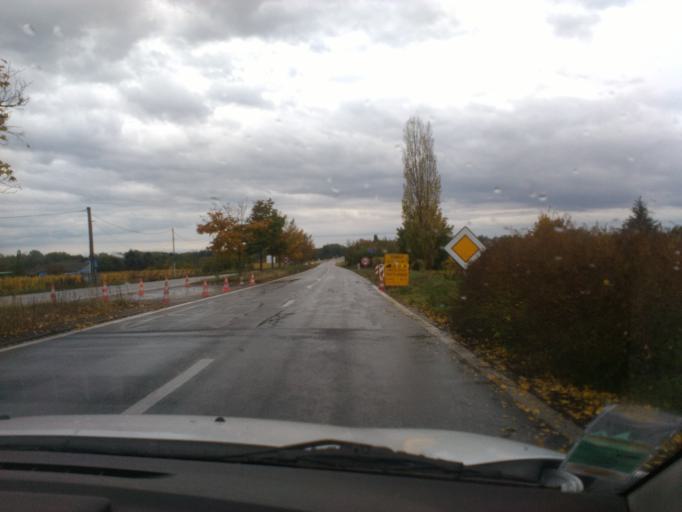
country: FR
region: Alsace
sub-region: Departement du Haut-Rhin
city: Ingersheim
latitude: 48.1033
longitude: 7.3037
